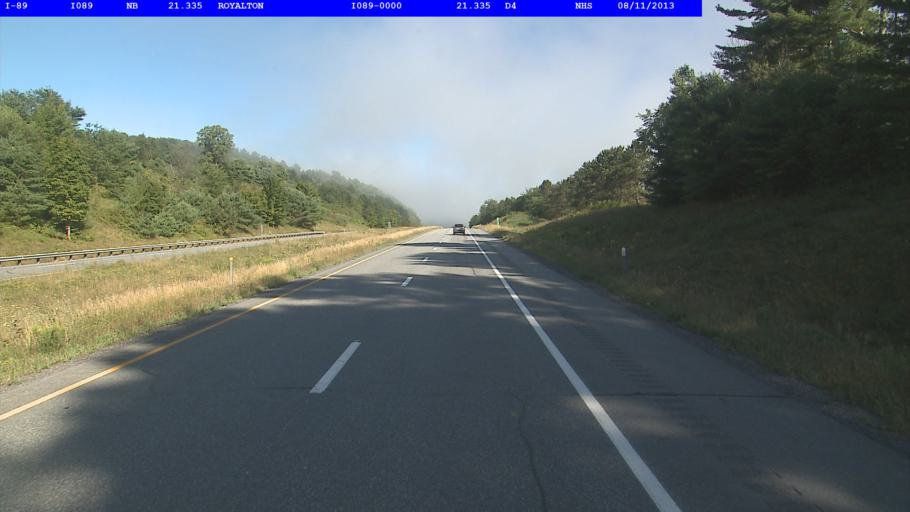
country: US
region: Vermont
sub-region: Orange County
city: Randolph
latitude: 43.8174
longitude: -72.5693
